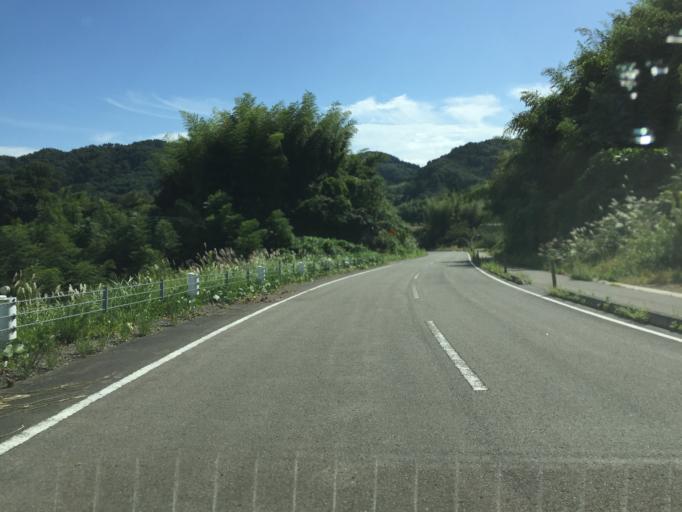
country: JP
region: Fukushima
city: Hobaramachi
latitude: 37.7774
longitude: 140.5412
